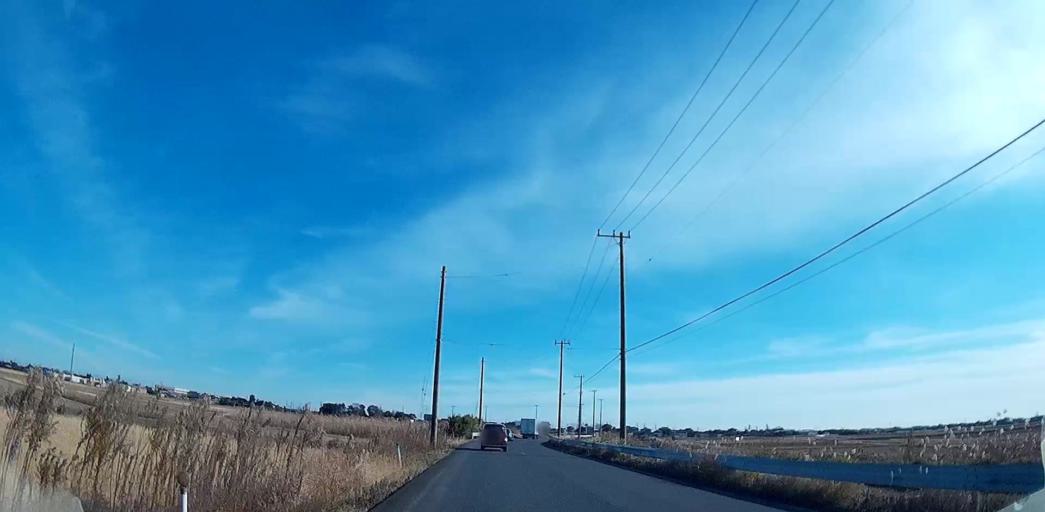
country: JP
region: Chiba
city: Yokaichiba
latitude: 35.7406
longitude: 140.5816
